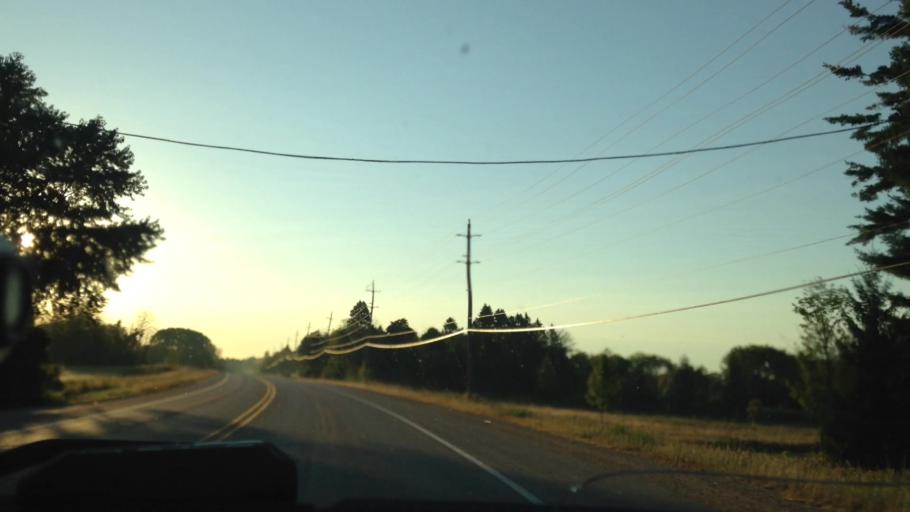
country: US
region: Wisconsin
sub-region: Washington County
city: Newburg
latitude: 43.4093
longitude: -88.0061
